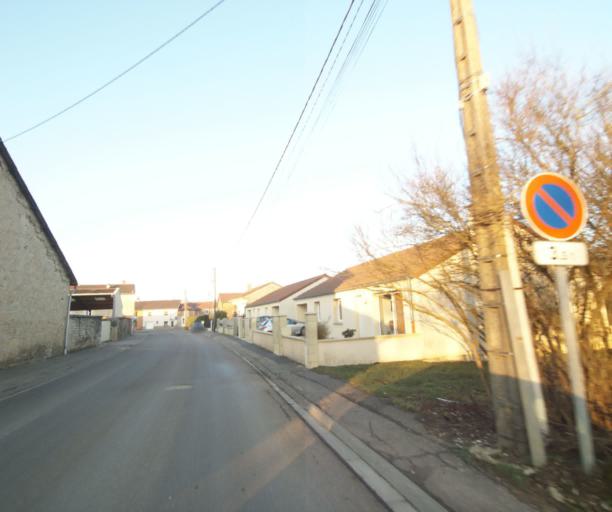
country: FR
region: Champagne-Ardenne
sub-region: Departement de la Haute-Marne
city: Bienville
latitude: 48.6027
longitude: 5.0446
